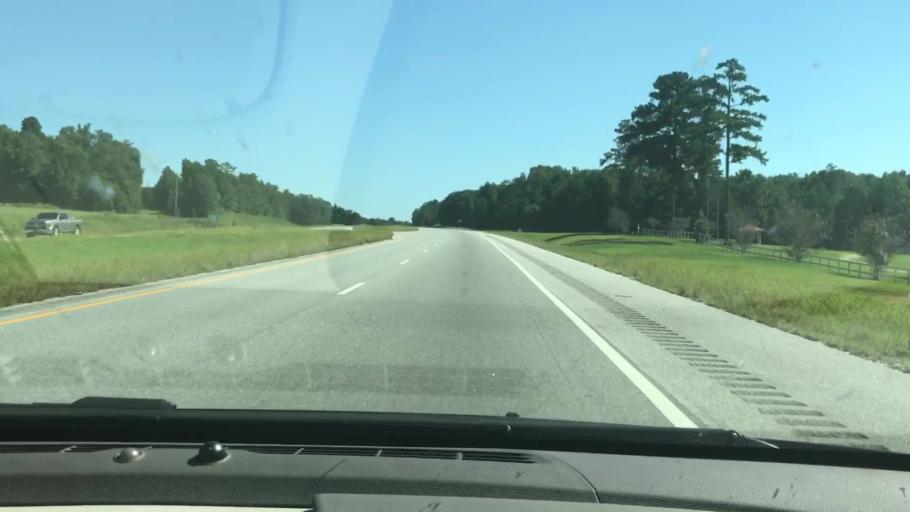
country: US
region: Alabama
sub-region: Russell County
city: Ladonia
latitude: 32.3962
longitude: -85.0673
